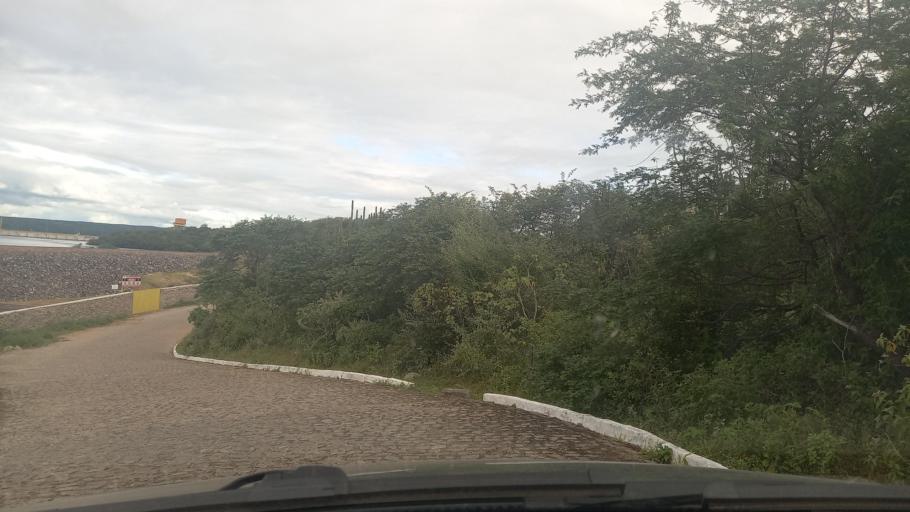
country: BR
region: Sergipe
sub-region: Caninde De Sao Francisco
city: Caninde de Sao Francisco
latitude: -9.6196
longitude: -37.8044
